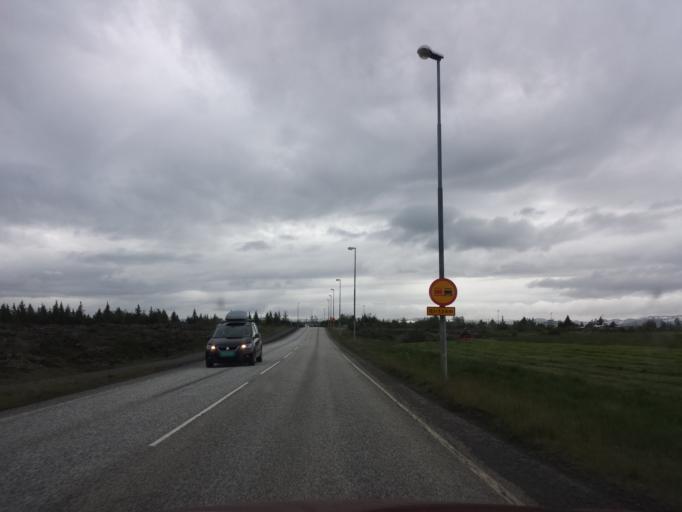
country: IS
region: Capital Region
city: Hafnarfjoerdur
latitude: 64.0860
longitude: -21.9730
